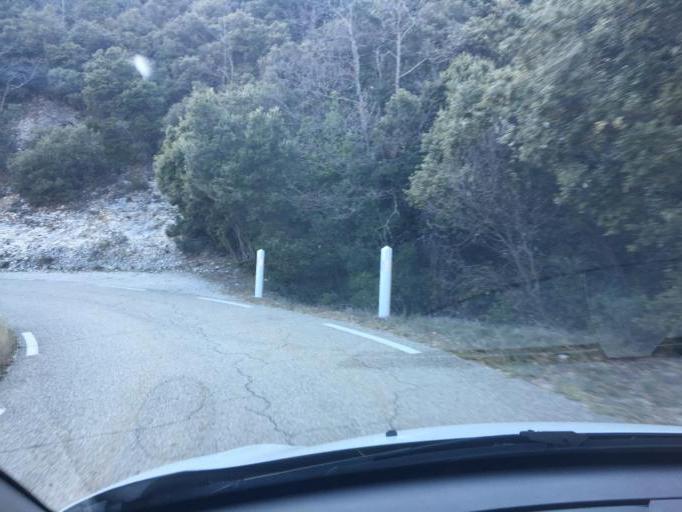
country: FR
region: Provence-Alpes-Cote d'Azur
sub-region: Departement du Vaucluse
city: Villes-sur-Auzon
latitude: 44.0473
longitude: 5.2752
